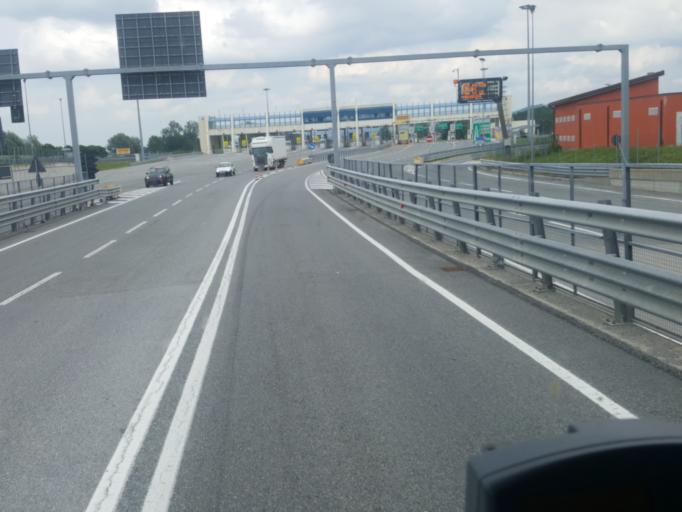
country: IT
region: Piedmont
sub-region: Provincia di Cuneo
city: Briaglia
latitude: 44.4226
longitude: 7.8504
